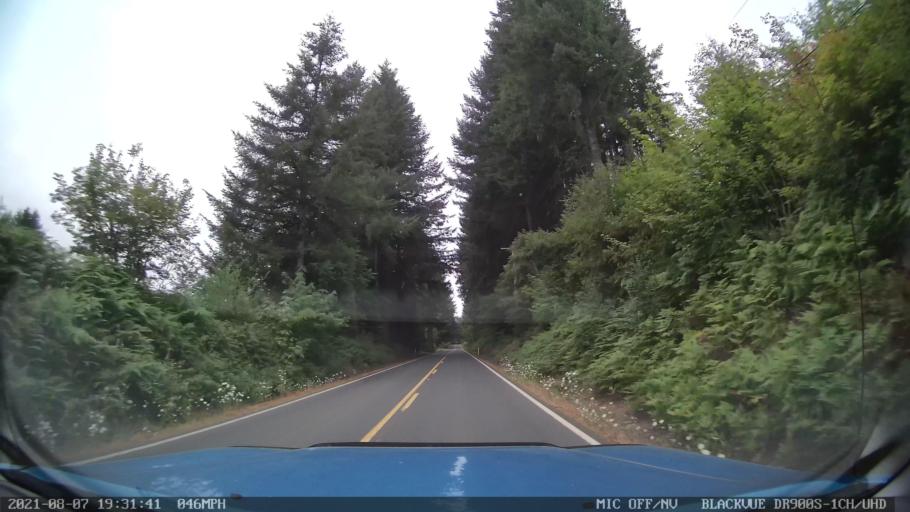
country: US
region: Oregon
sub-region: Linn County
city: Lyons
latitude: 44.8936
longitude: -122.6362
